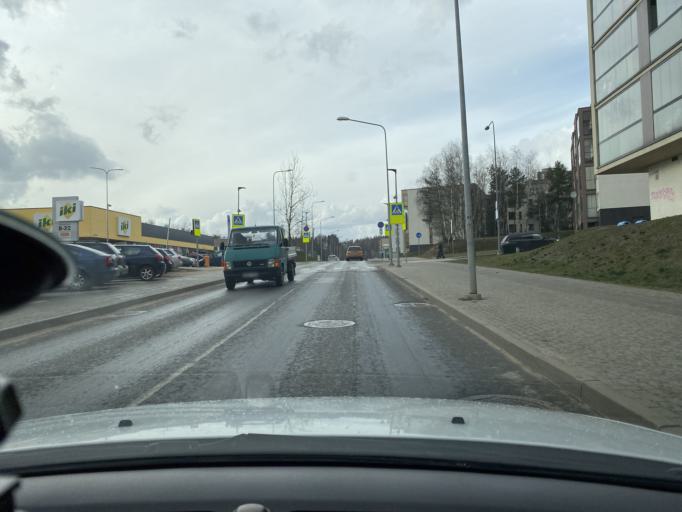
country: LT
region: Vilnius County
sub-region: Vilnius
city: Fabijoniskes
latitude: 54.7544
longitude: 25.2630
